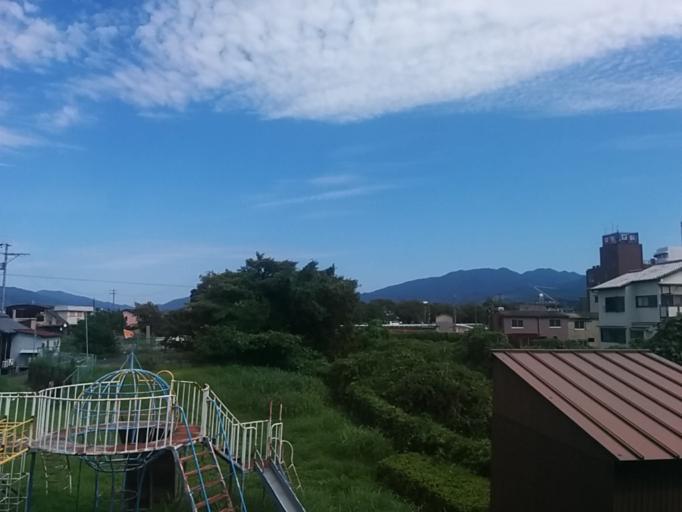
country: JP
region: Nara
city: Kashihara-shi
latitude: 34.5066
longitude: 135.7909
